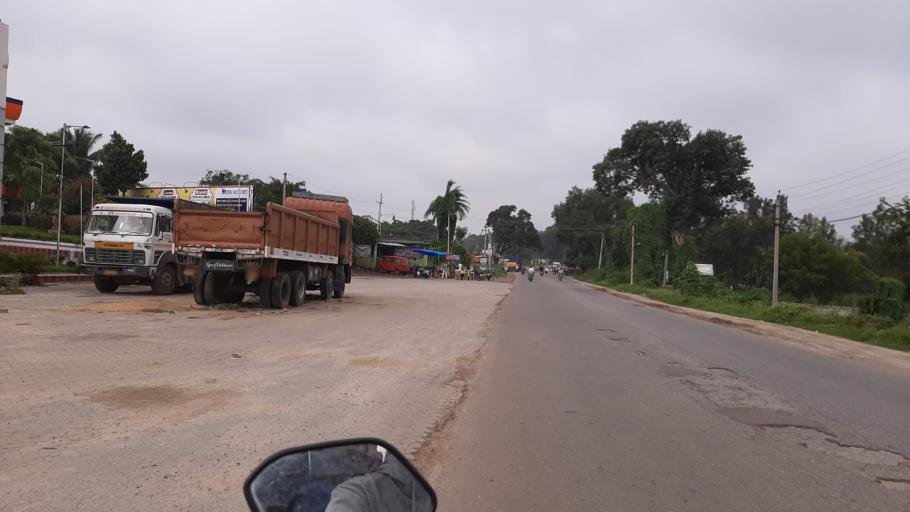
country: IN
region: Karnataka
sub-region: Bangalore Rural
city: Nelamangala
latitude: 12.9716
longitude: 77.4161
